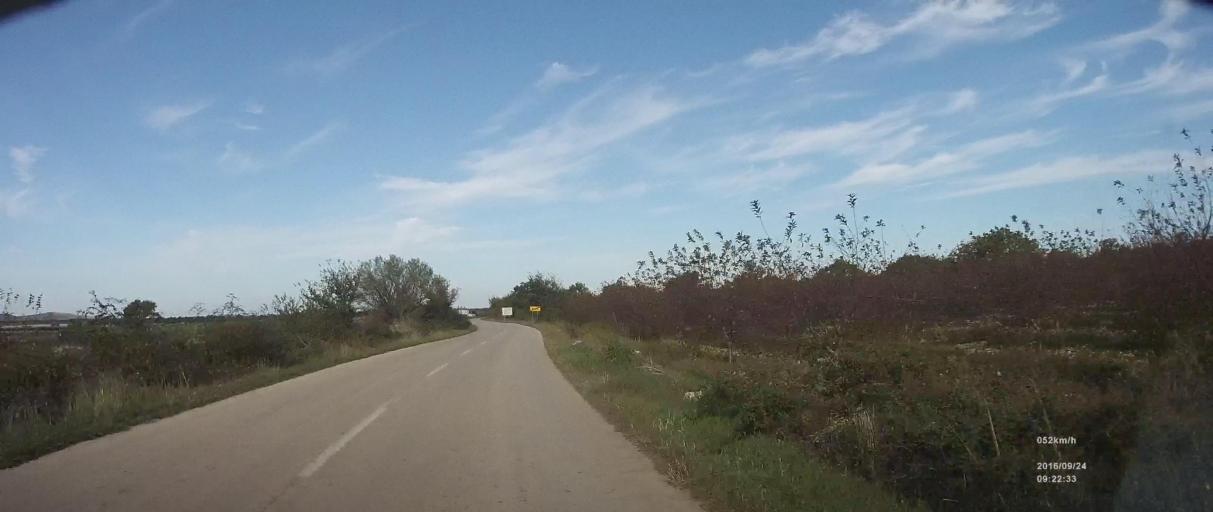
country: HR
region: Zadarska
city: Polaca
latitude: 44.0699
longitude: 15.4794
